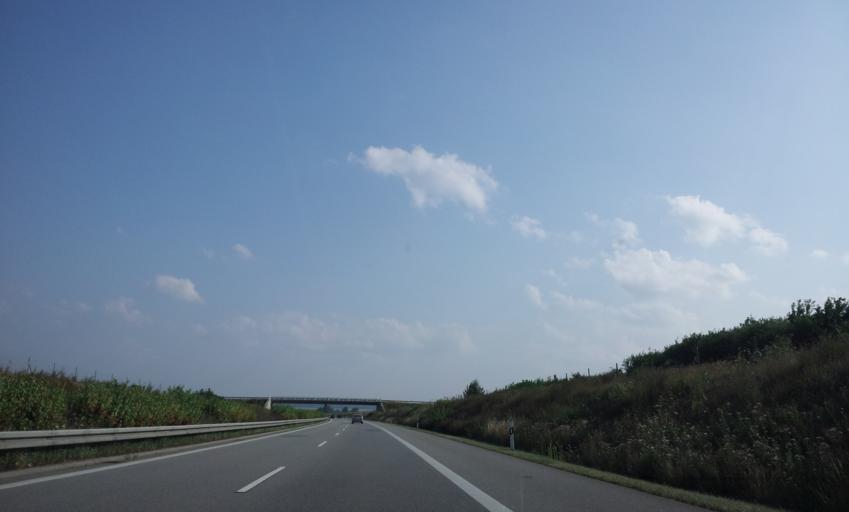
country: DE
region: Mecklenburg-Vorpommern
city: Kessin
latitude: 53.6991
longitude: 13.3257
